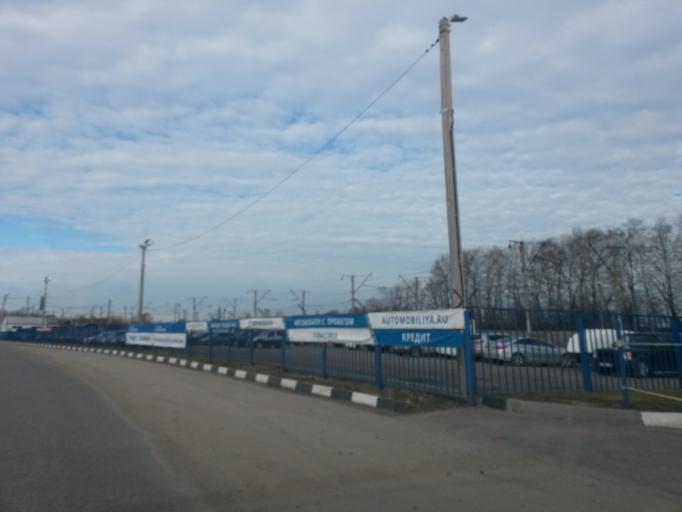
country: RU
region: Jaroslavl
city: Yaroslavl
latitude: 57.6438
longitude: 39.8106
